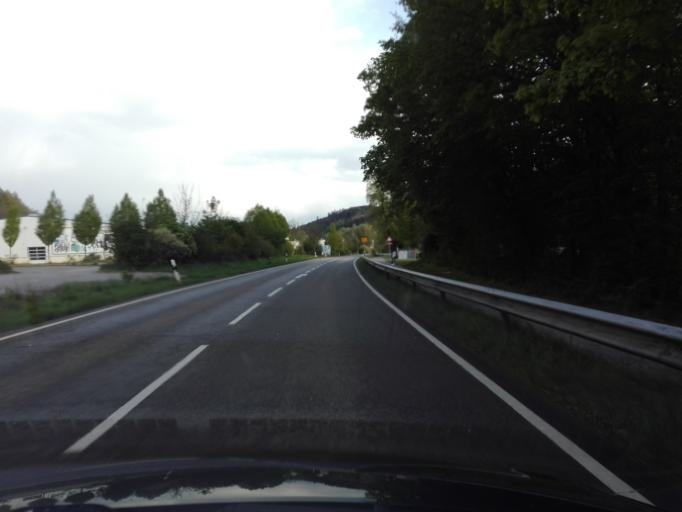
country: DE
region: Bavaria
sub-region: Lower Bavaria
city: Obernzell
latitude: 48.5601
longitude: 13.6210
